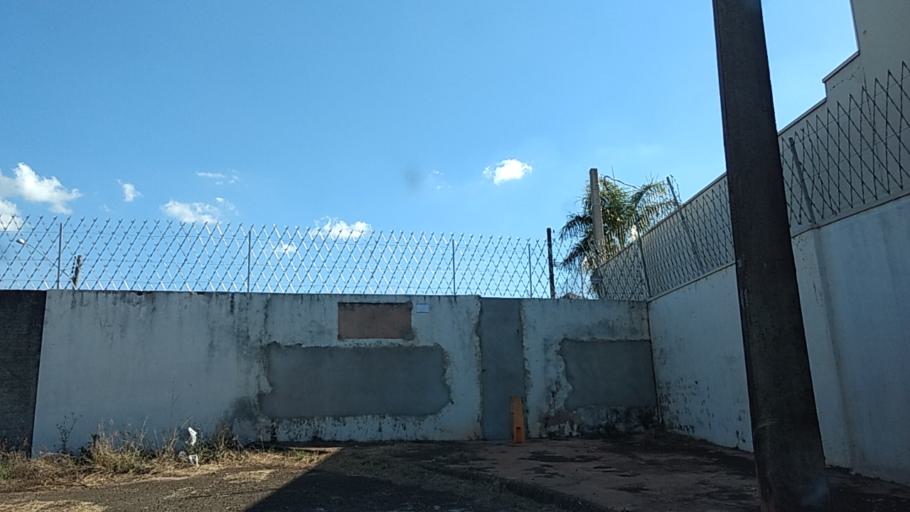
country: BR
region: Sao Paulo
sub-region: Botucatu
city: Botucatu
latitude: -22.8546
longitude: -48.4375
